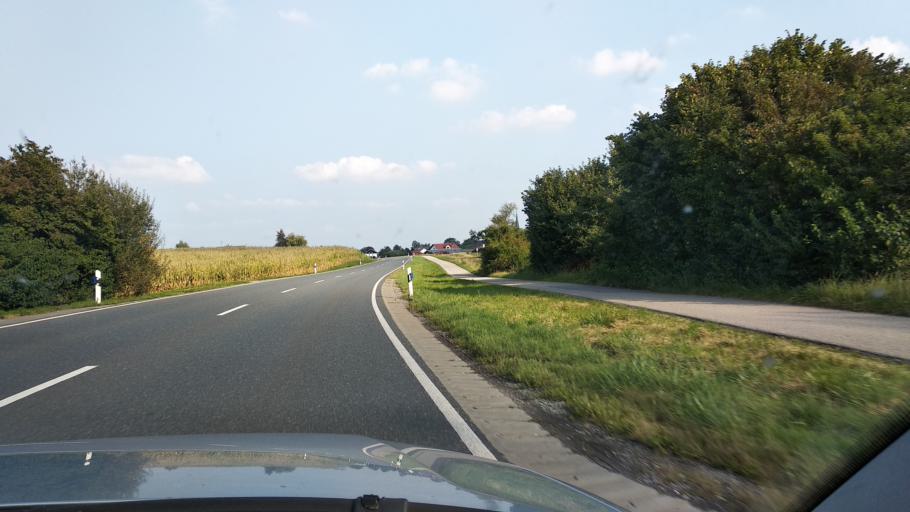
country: DE
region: Bavaria
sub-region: Upper Bavaria
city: Steinhoring
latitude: 48.0843
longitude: 12.0528
